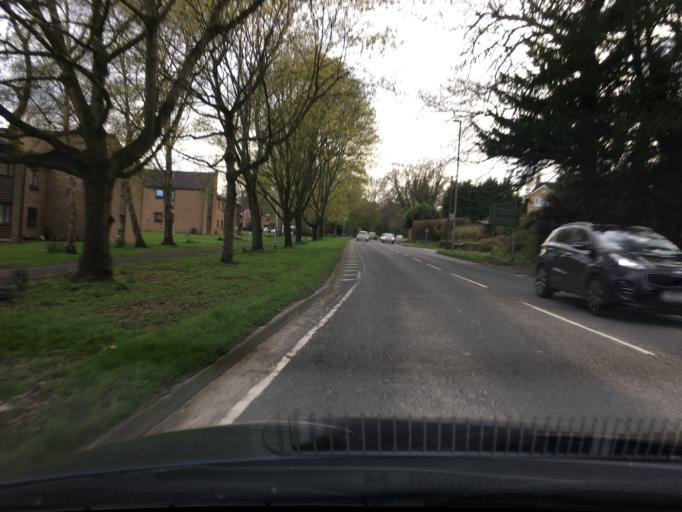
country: GB
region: England
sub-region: Hampshire
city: Yateley
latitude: 51.3384
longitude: -0.8169
